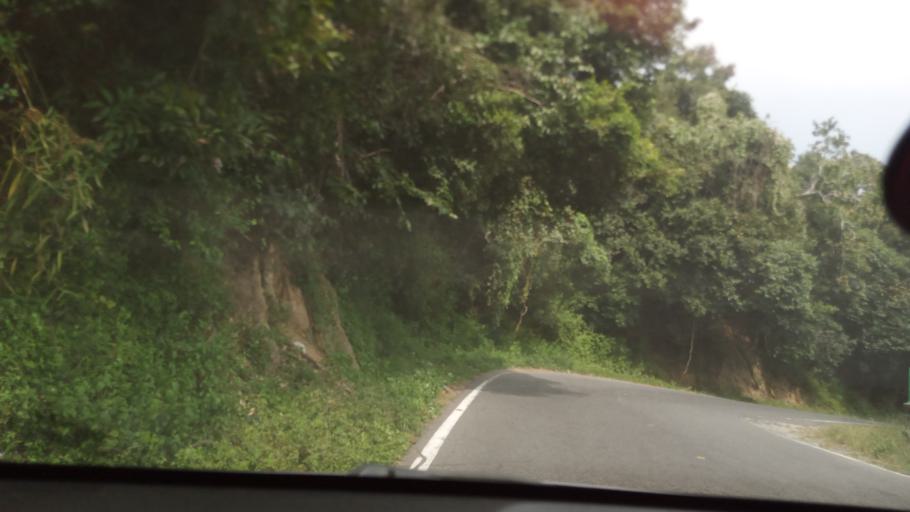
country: IN
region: Tamil Nadu
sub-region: Erode
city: Sathyamangalam
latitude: 11.5981
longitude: 77.1248
